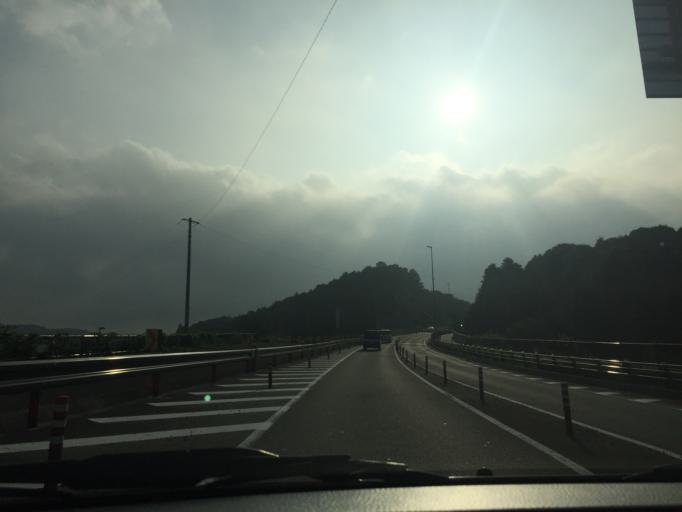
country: JP
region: Aichi
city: Shinshiro
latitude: 34.9164
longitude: 137.5330
